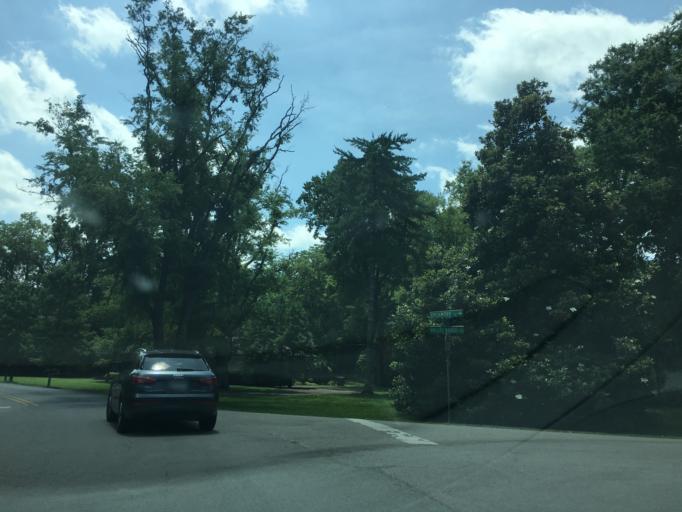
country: US
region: Tennessee
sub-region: Davidson County
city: Belle Meade
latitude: 36.1119
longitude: -86.8257
